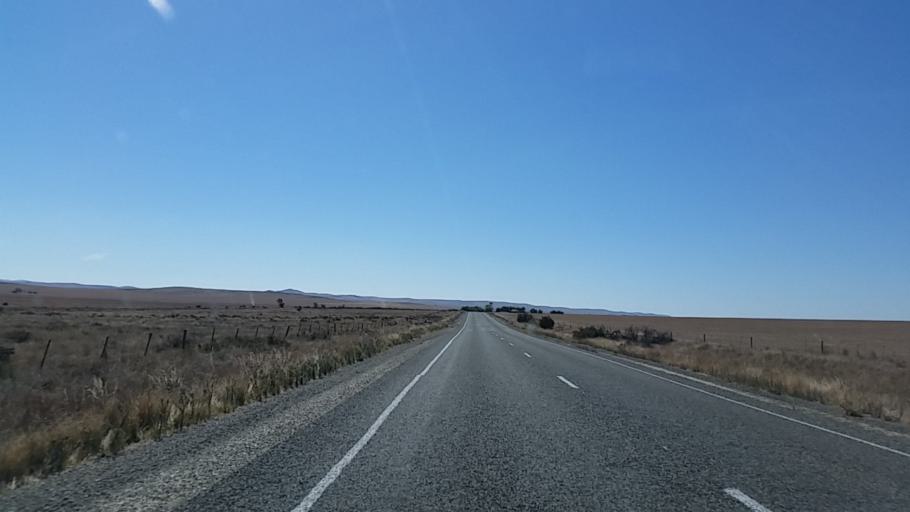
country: AU
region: South Australia
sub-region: Northern Areas
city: Jamestown
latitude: -33.2897
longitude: 138.8712
